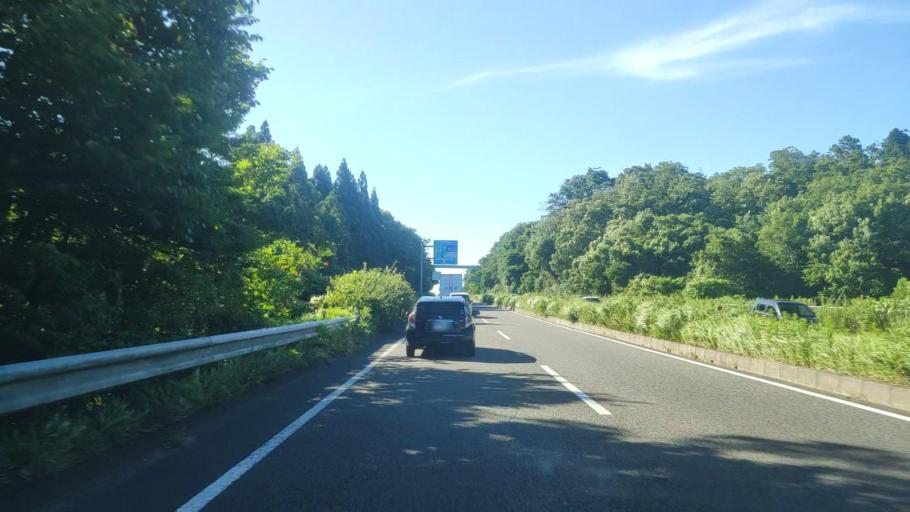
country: JP
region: Shiga Prefecture
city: Minakuchicho-matoba
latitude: 34.9692
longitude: 136.1935
